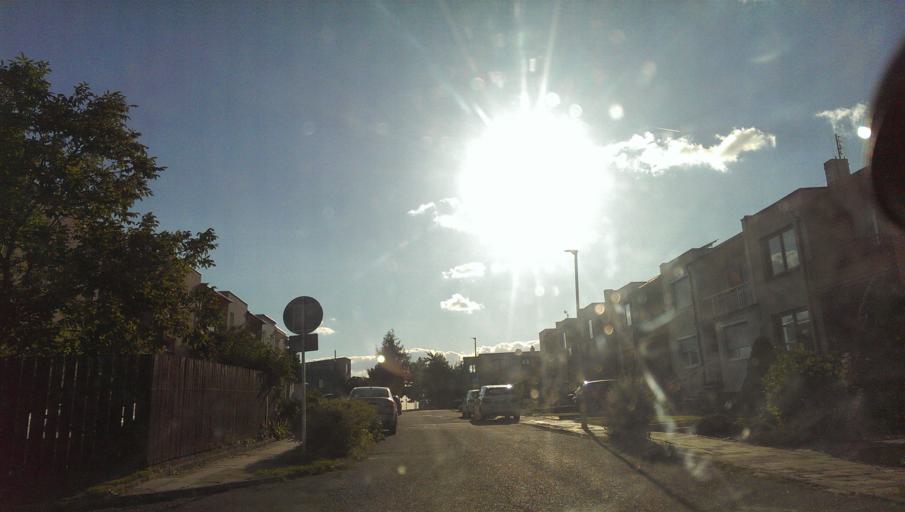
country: CZ
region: Zlin
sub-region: Okres Uherske Hradiste
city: Uherske Hradiste
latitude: 49.0633
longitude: 17.4771
